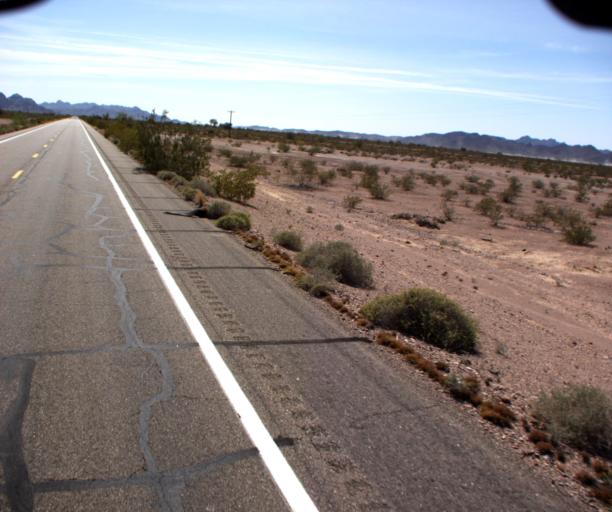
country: US
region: Arizona
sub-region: La Paz County
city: Quartzsite
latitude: 33.3585
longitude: -114.2171
